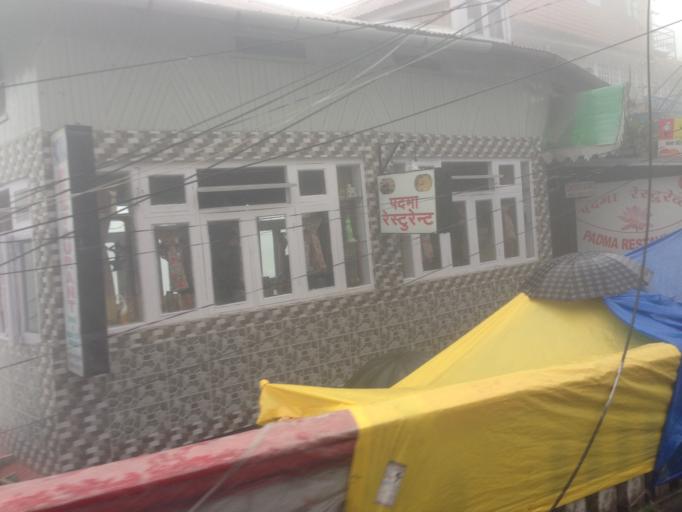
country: IN
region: West Bengal
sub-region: Darjiling
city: Darjiling
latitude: 27.0418
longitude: 88.2665
